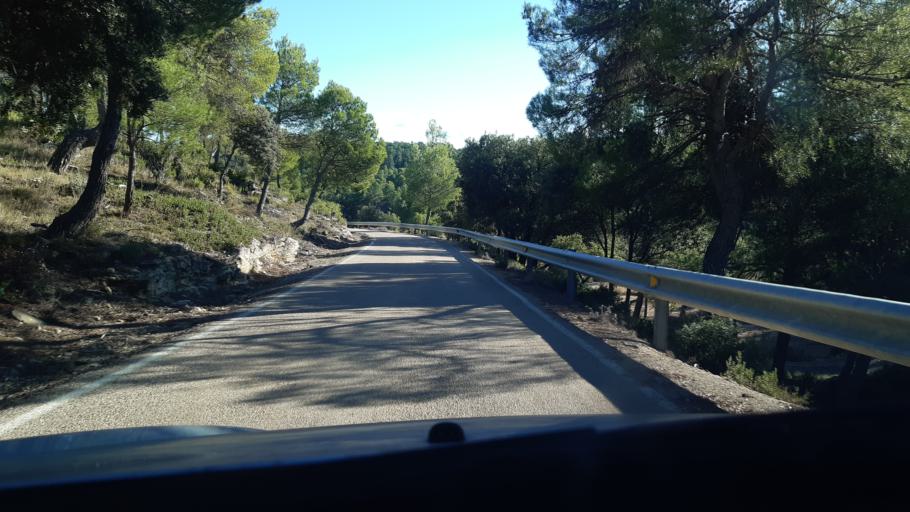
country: ES
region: Aragon
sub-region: Provincia de Teruel
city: Fornoles
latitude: 40.9116
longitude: -0.0178
